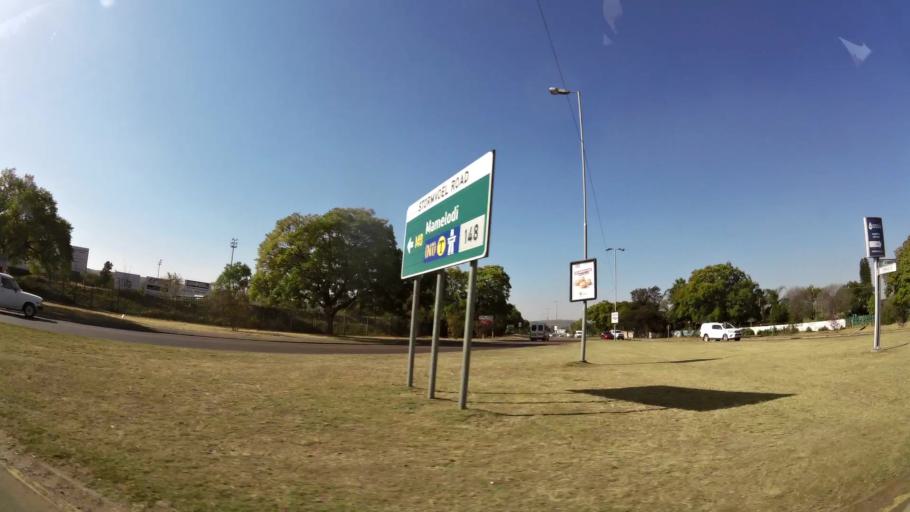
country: ZA
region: Gauteng
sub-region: City of Tshwane Metropolitan Municipality
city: Pretoria
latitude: -25.7122
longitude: 28.2578
